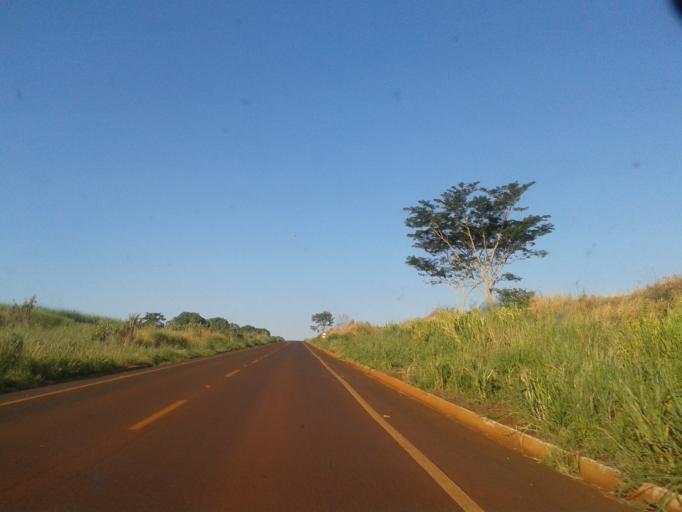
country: BR
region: Minas Gerais
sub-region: Capinopolis
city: Capinopolis
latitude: -18.7074
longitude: -49.6997
